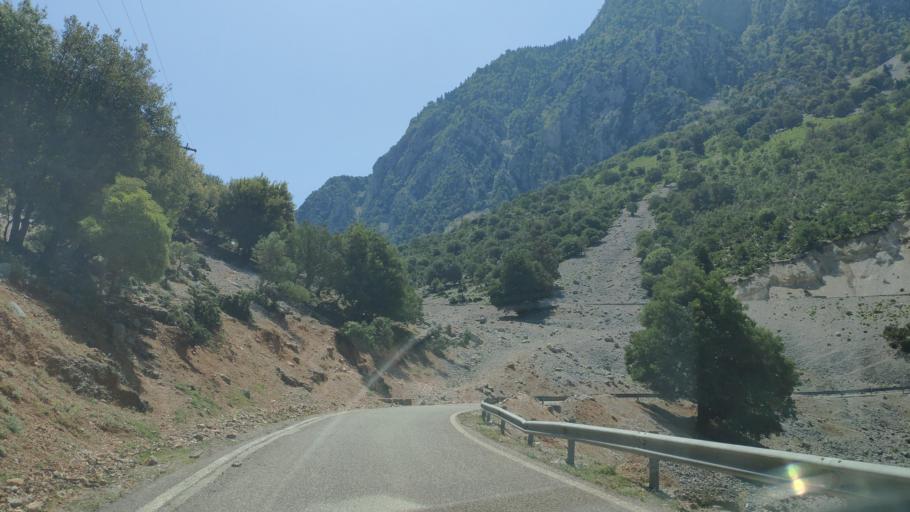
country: GR
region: West Greece
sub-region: Nomos Aitolias kai Akarnanias
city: Krikellos
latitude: 39.0217
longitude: 21.3372
